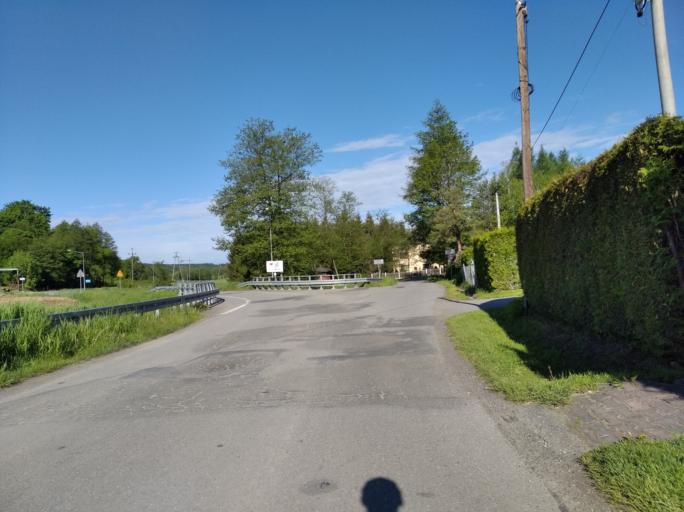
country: PL
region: Subcarpathian Voivodeship
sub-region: Powiat strzyzowski
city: Frysztak
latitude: 49.8332
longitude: 21.6019
